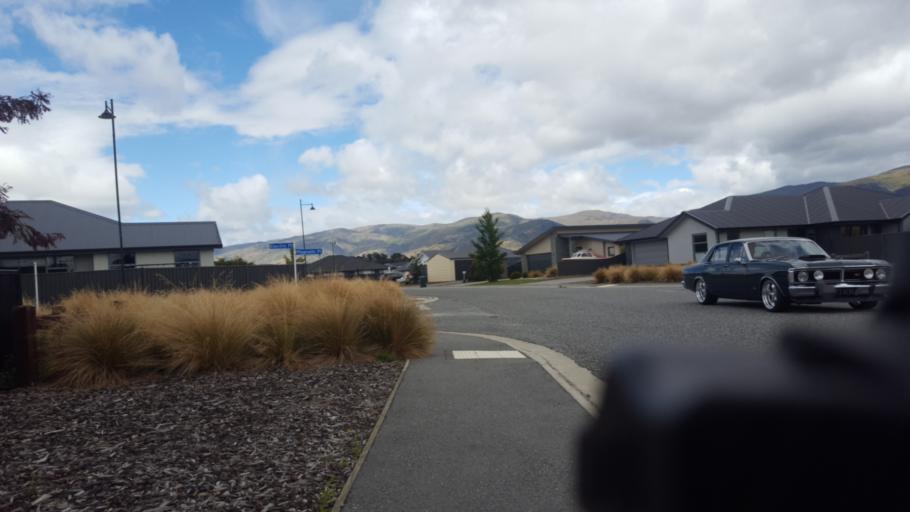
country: NZ
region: Otago
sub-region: Queenstown-Lakes District
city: Wanaka
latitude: -45.0464
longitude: 169.1802
